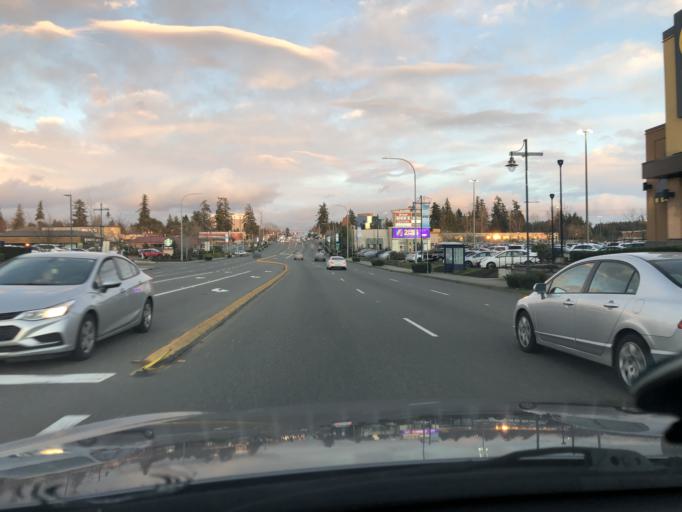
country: US
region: Washington
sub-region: King County
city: Federal Way
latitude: 47.3150
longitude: -122.3084
